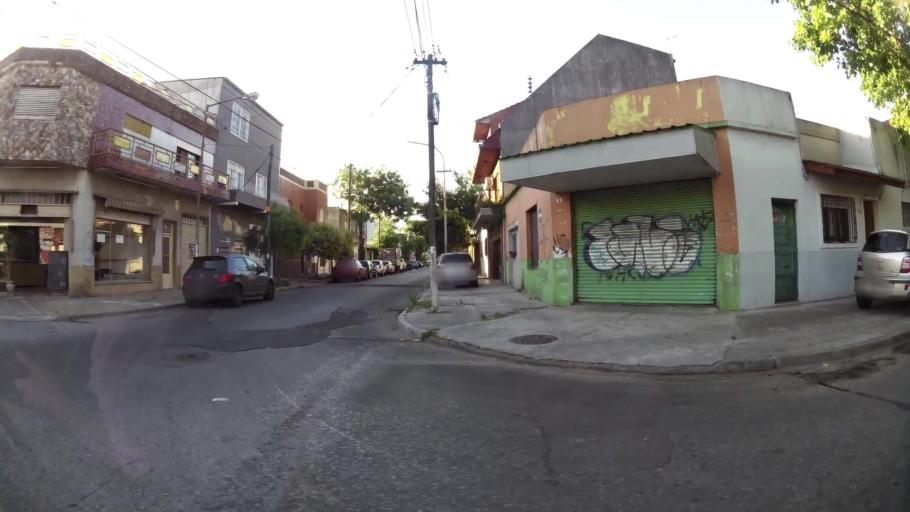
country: AR
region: Buenos Aires
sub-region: Partido de General San Martin
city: General San Martin
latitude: -34.5707
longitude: -58.5497
